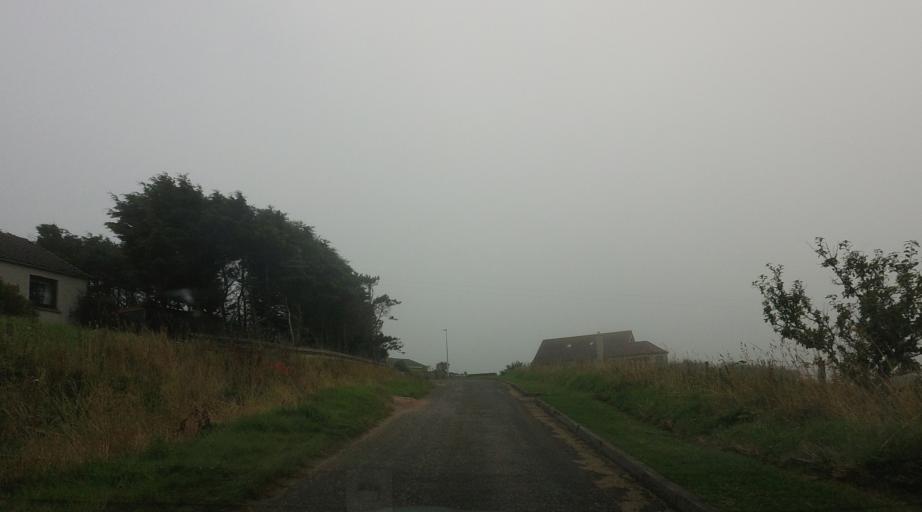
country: GB
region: Scotland
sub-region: Highland
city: Wick
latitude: 58.2996
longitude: -3.2876
